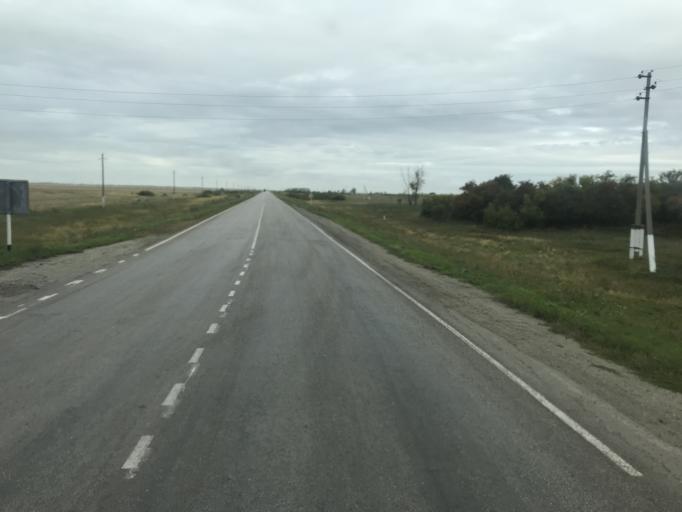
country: KZ
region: Qostanay
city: Komsomolets
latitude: 53.8759
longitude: 61.9584
